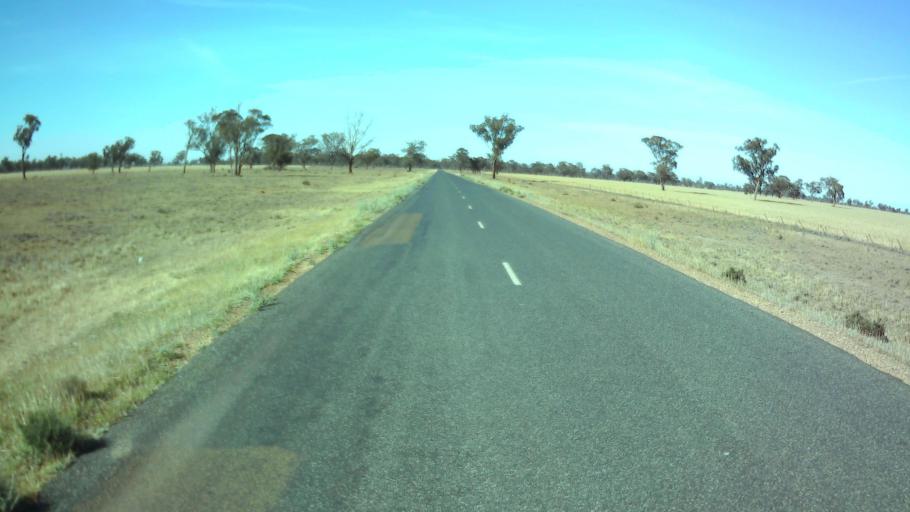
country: AU
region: New South Wales
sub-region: Weddin
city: Grenfell
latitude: -34.0514
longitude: 147.9187
